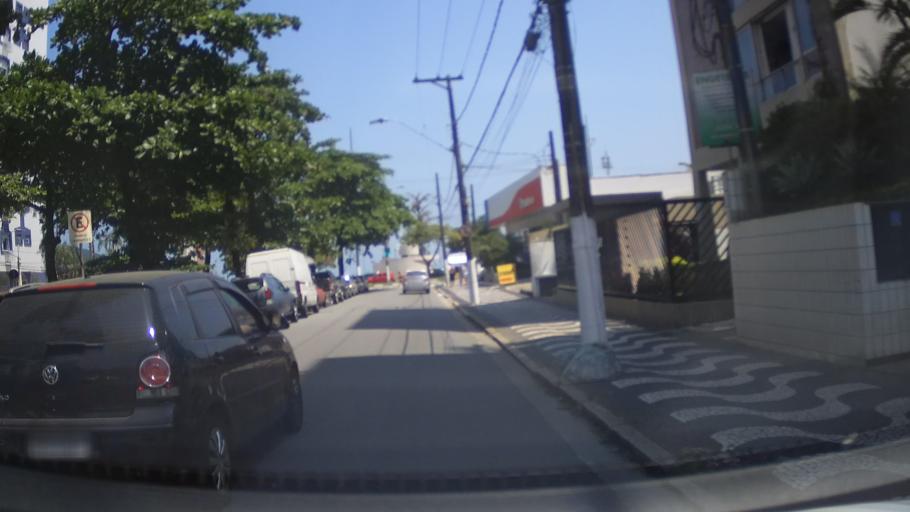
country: BR
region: Sao Paulo
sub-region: Santos
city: Santos
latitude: -23.9832
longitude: -46.3087
